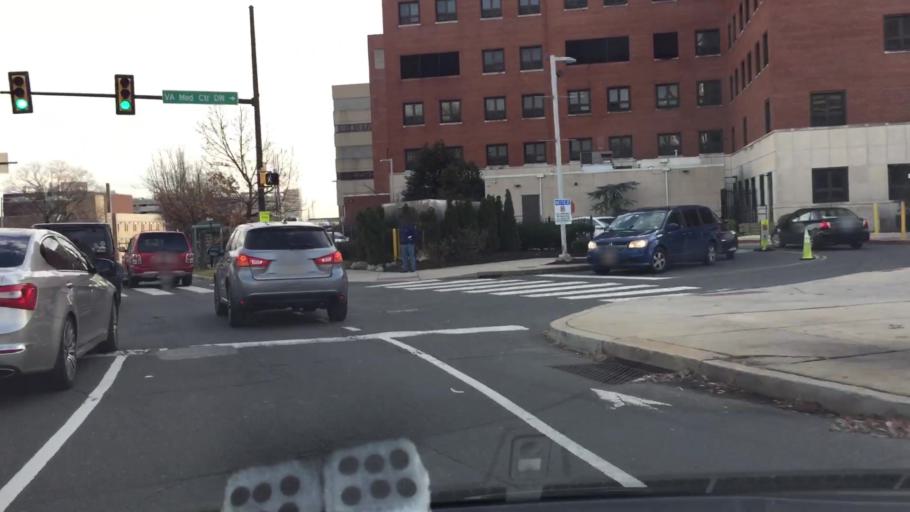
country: US
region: Pennsylvania
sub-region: Philadelphia County
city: Philadelphia
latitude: 39.9501
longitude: -75.1997
